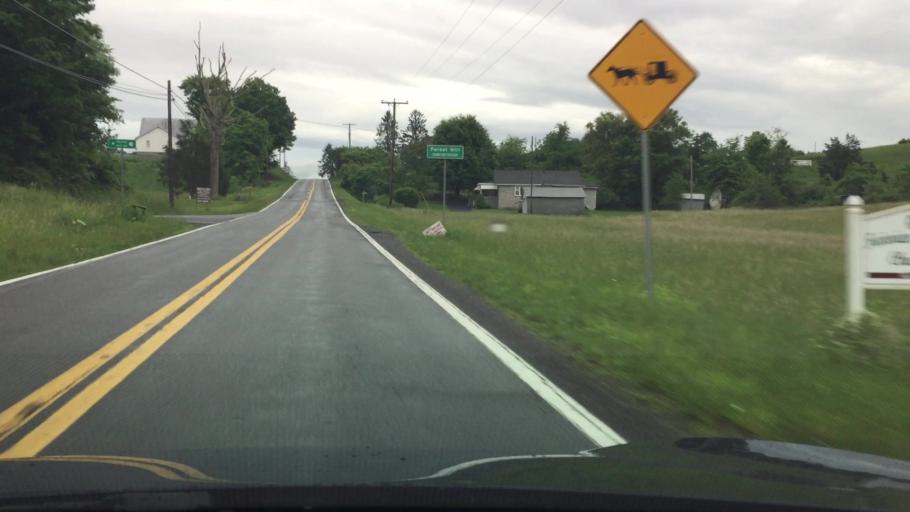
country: US
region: West Virginia
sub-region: Summers County
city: Hinton
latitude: 37.5723
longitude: -80.7888
